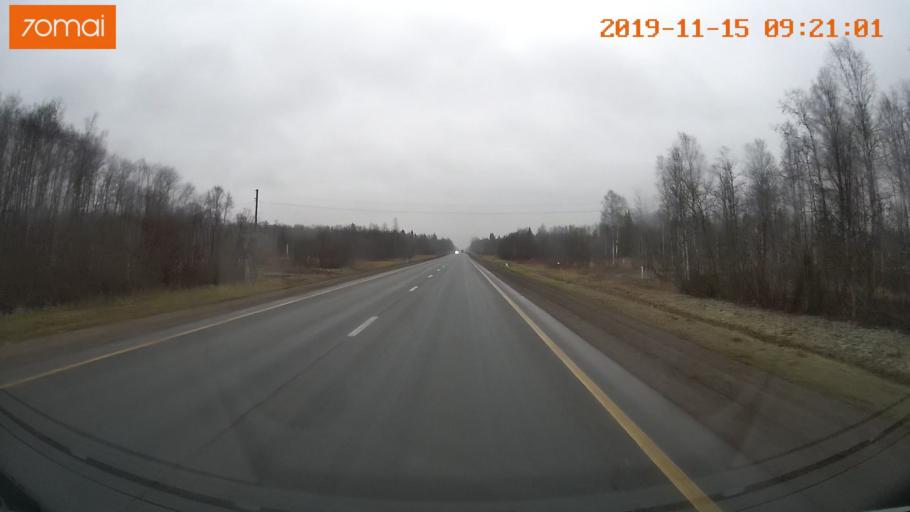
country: RU
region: Vologda
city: Tonshalovo
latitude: 59.2930
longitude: 38.0528
